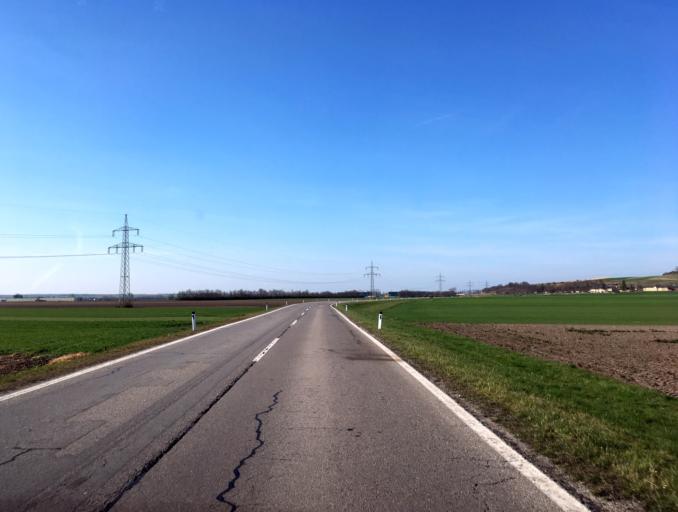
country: AT
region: Lower Austria
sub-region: Politischer Bezirk Bruck an der Leitha
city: Enzersdorf an der Fischa
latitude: 48.0521
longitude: 16.6181
